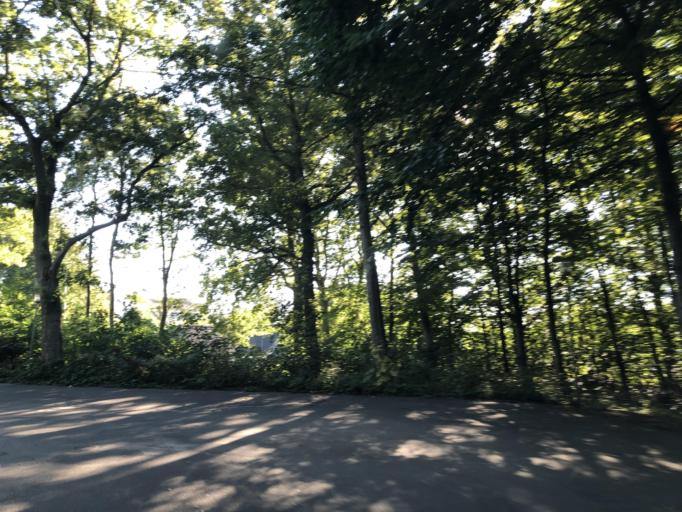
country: DK
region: North Denmark
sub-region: Mariagerfjord Kommune
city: Hobro
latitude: 56.6347
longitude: 9.8301
